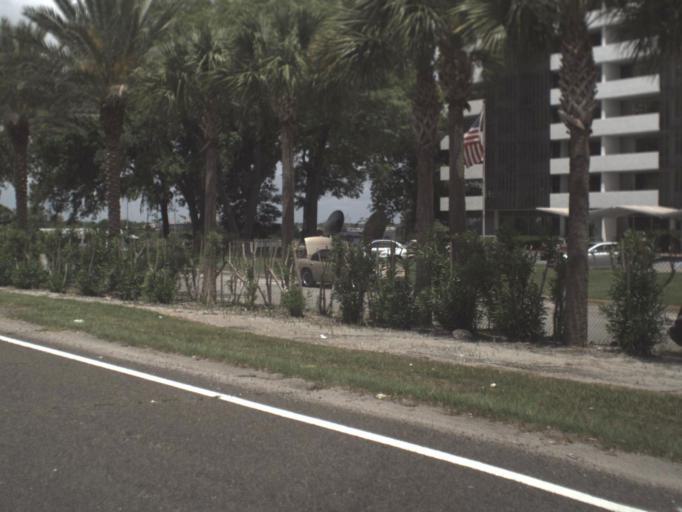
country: US
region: Florida
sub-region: Duval County
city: Jacksonville
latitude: 30.3274
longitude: -81.6099
